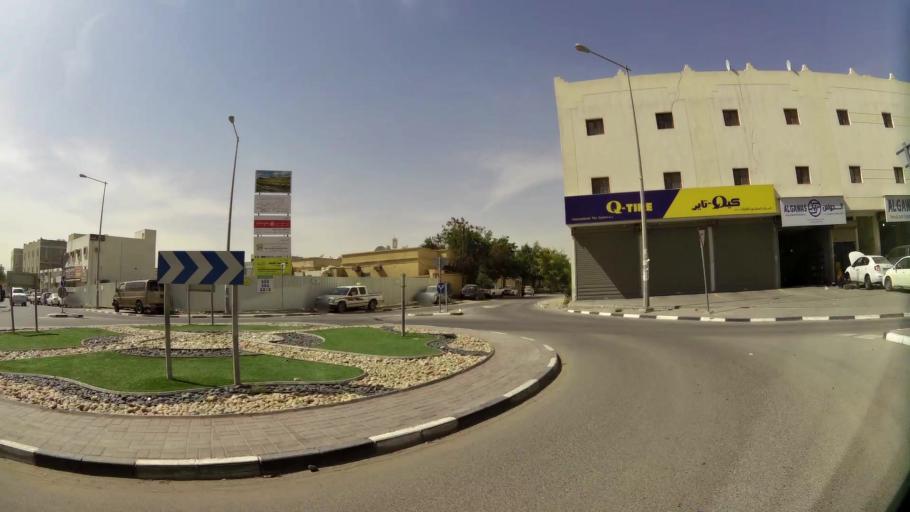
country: QA
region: Baladiyat ar Rayyan
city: Ar Rayyan
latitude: 25.2729
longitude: 51.4125
